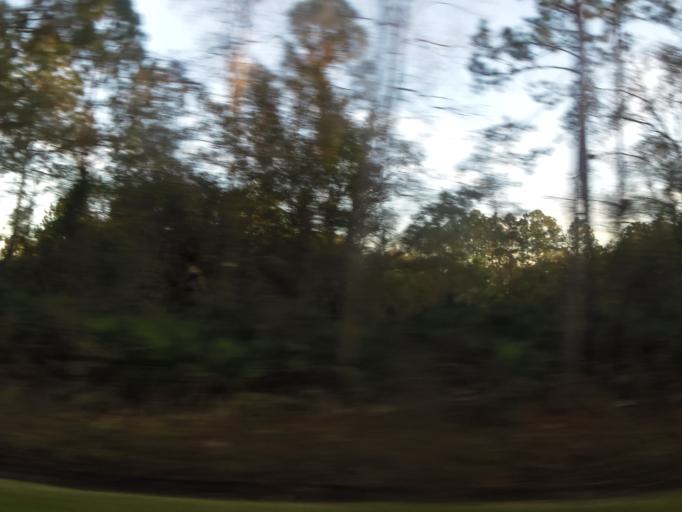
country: US
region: Florida
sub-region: Clay County
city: Green Cove Springs
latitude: 29.9509
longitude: -81.5524
